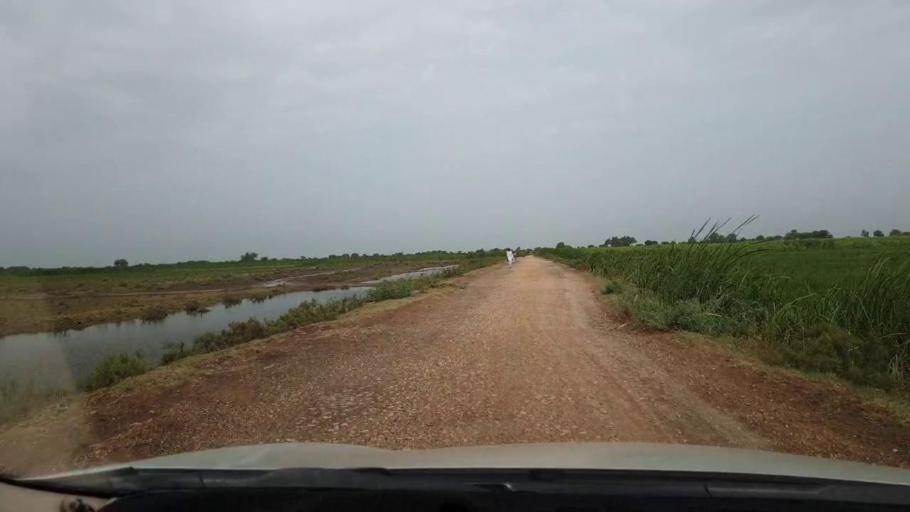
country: PK
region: Sindh
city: Matli
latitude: 25.1040
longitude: 68.6227
